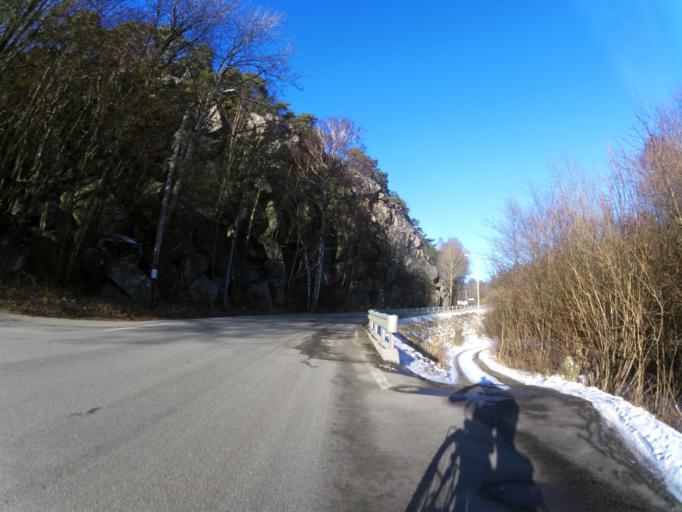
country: NO
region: Ostfold
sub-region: Fredrikstad
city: Lervik
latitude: 59.2199
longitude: 10.7924
